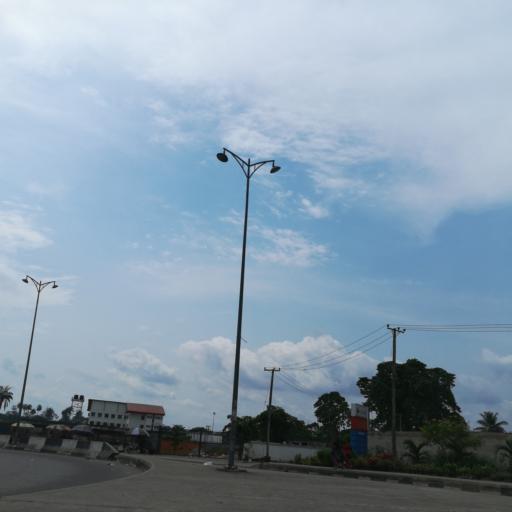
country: NG
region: Rivers
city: Port Harcourt
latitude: 4.8393
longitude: 7.0145
